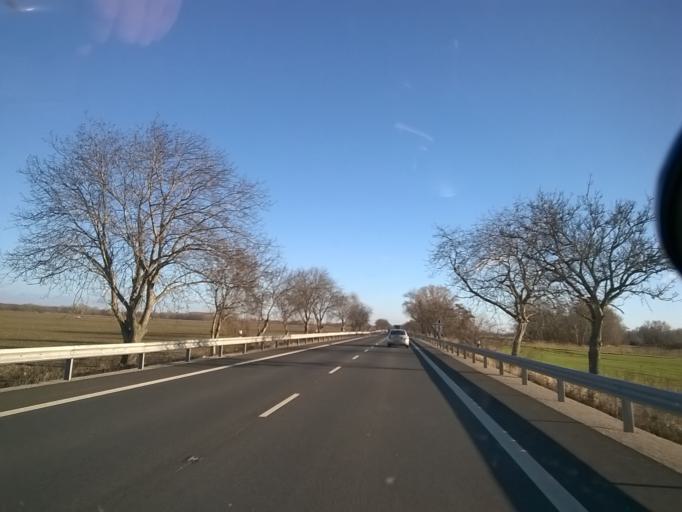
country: SK
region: Trnavsky
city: Sladkovicovo
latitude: 48.2011
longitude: 17.5587
